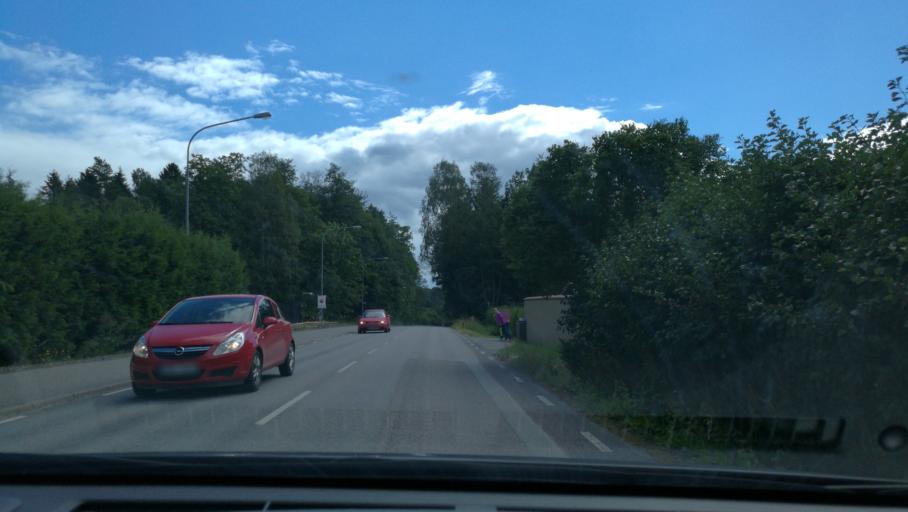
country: SE
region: OEstergoetland
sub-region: Norrkopings Kommun
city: Krokek
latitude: 58.6683
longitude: 16.3695
